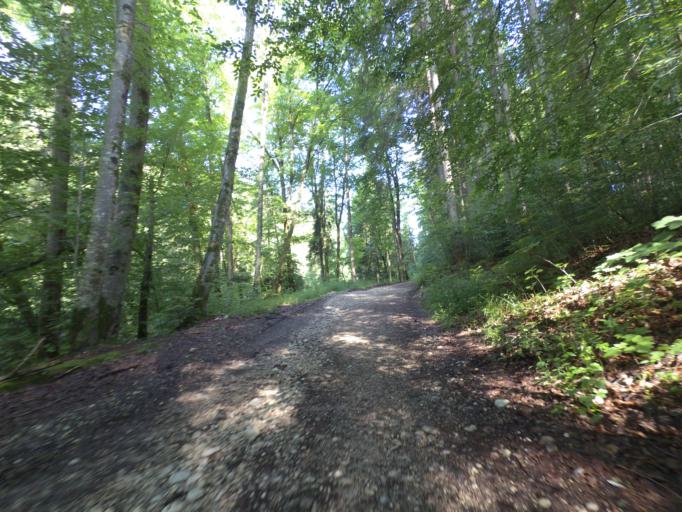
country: AT
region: Salzburg
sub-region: Politischer Bezirk Salzburg-Umgebung
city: Grodig
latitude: 47.7517
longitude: 12.9920
